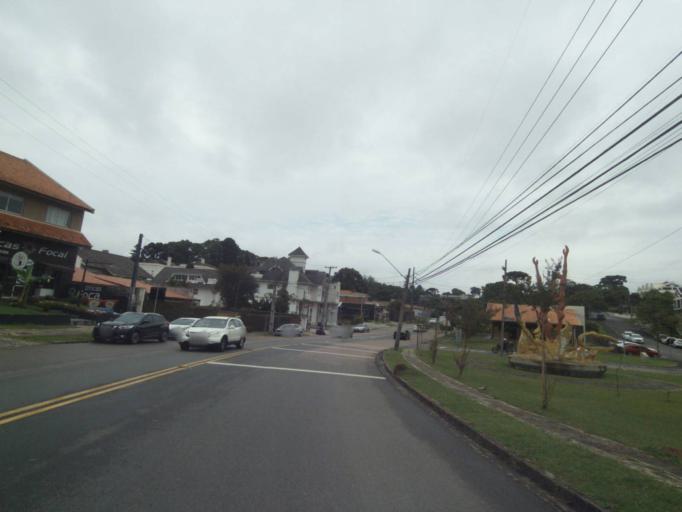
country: BR
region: Parana
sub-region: Curitiba
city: Curitiba
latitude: -25.4083
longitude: -49.2830
